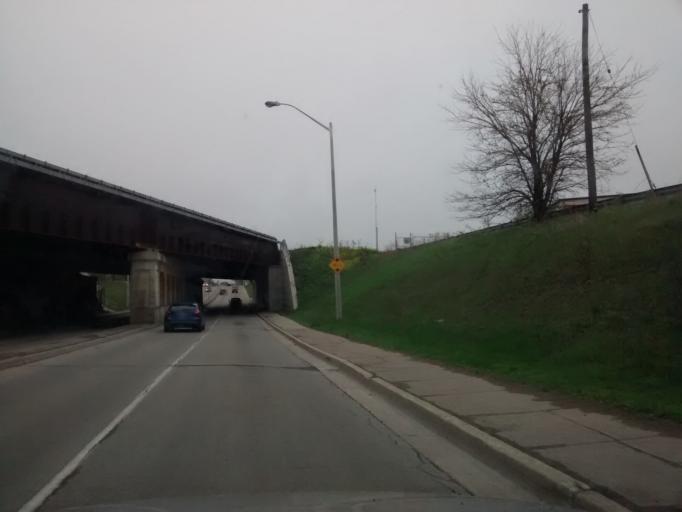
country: CA
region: Ontario
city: Burlington
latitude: 43.3332
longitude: -79.8215
